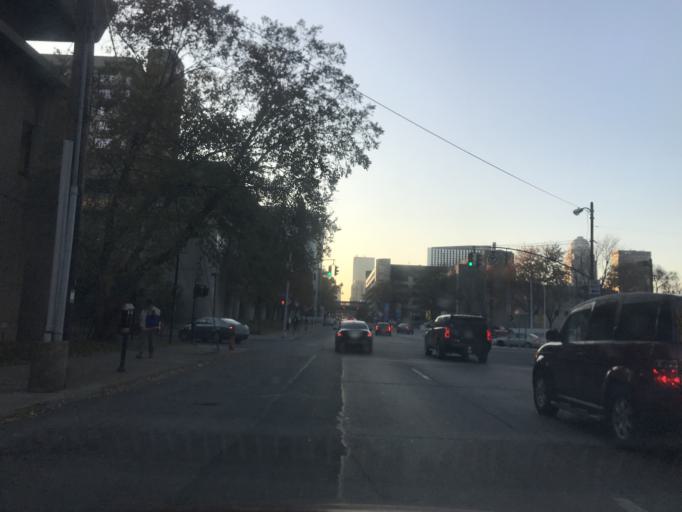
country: US
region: Kentucky
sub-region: Jefferson County
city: Louisville
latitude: 38.2499
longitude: -85.7464
